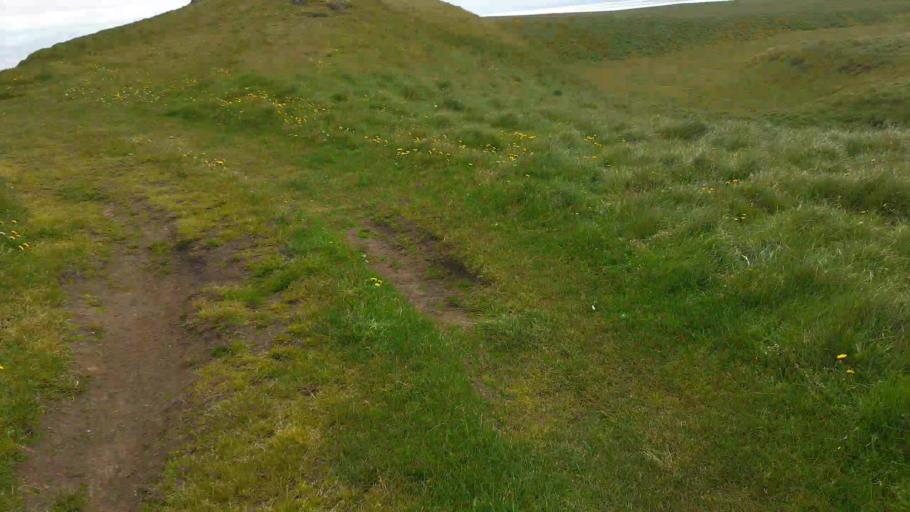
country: IS
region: Northeast
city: Dalvik
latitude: 66.5438
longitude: -17.9862
